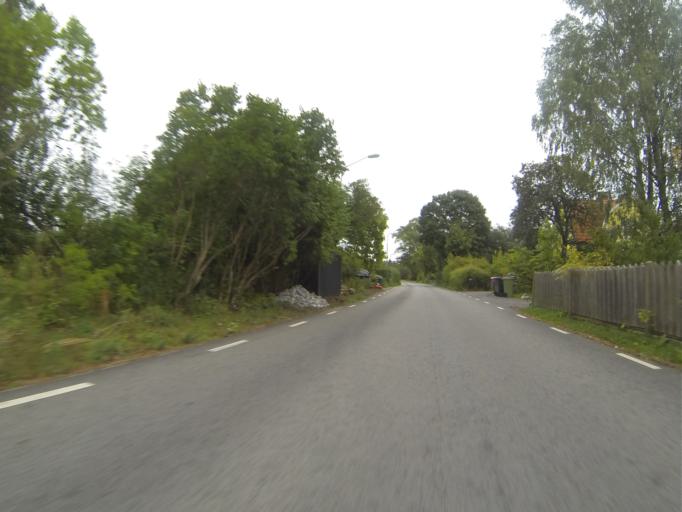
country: SE
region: Skane
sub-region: Lunds Kommun
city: Veberod
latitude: 55.6791
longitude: 13.4219
